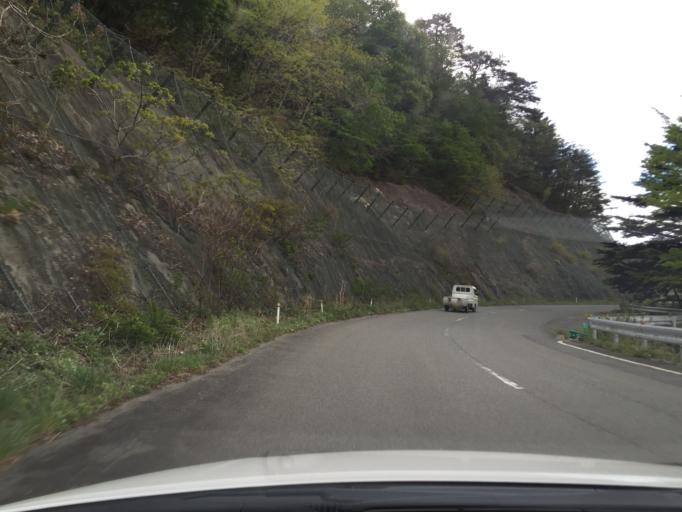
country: JP
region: Miyagi
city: Marumori
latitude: 37.7222
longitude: 140.7997
